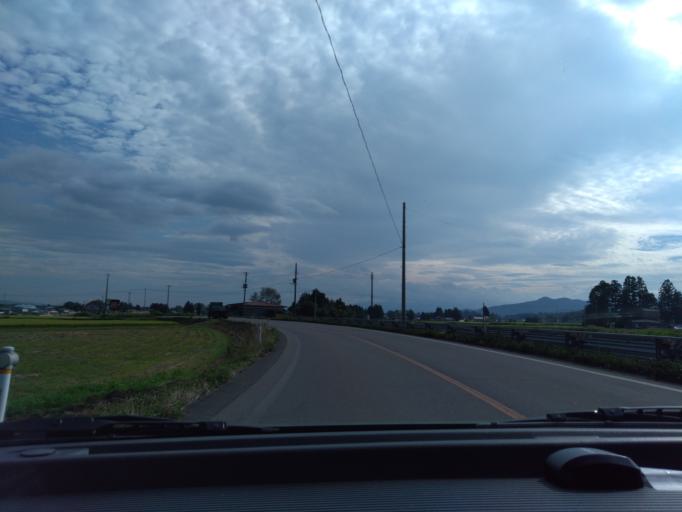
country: JP
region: Iwate
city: Hanamaki
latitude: 39.4671
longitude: 141.1013
